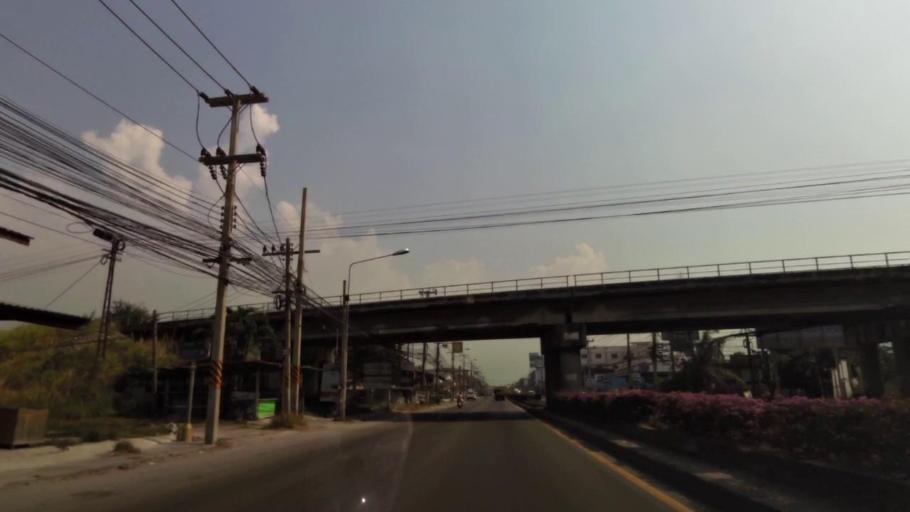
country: TH
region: Chon Buri
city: Chon Buri
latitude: 13.3520
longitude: 101.0074
